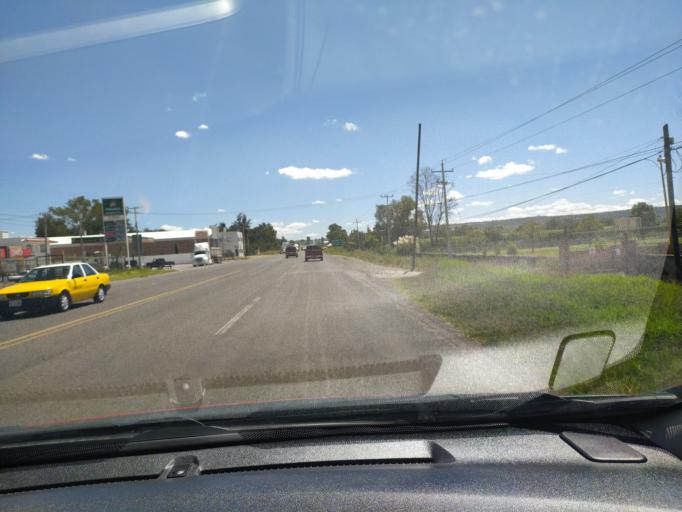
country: MX
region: Jalisco
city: San Miguel el Alto
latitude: 21.0285
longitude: -102.3830
